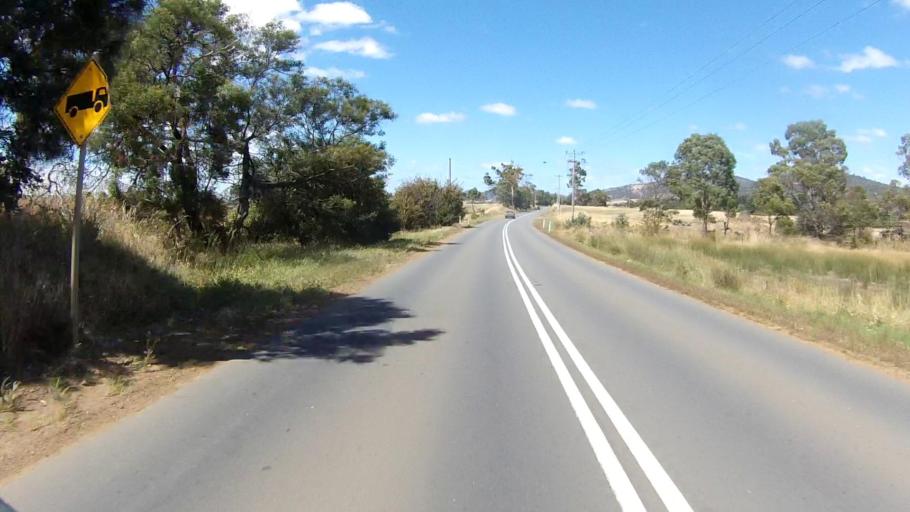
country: AU
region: Tasmania
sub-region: Clarence
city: Cambridge
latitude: -42.7664
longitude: 147.4156
